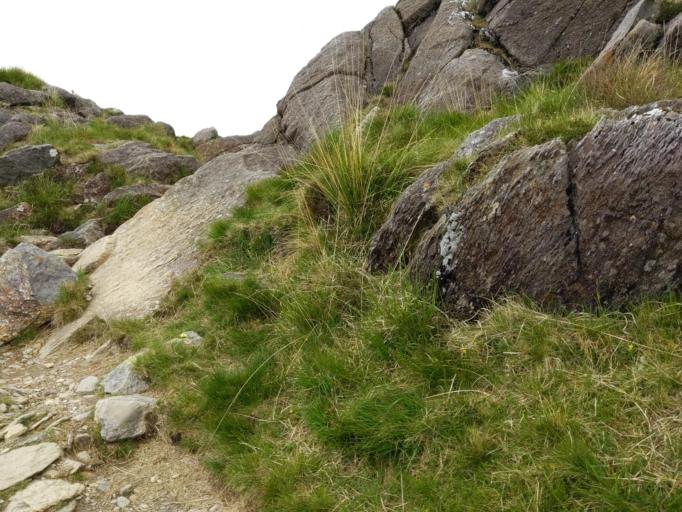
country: GB
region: Wales
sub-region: Gwynedd
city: Llanberis
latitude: 53.0525
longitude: -4.1125
